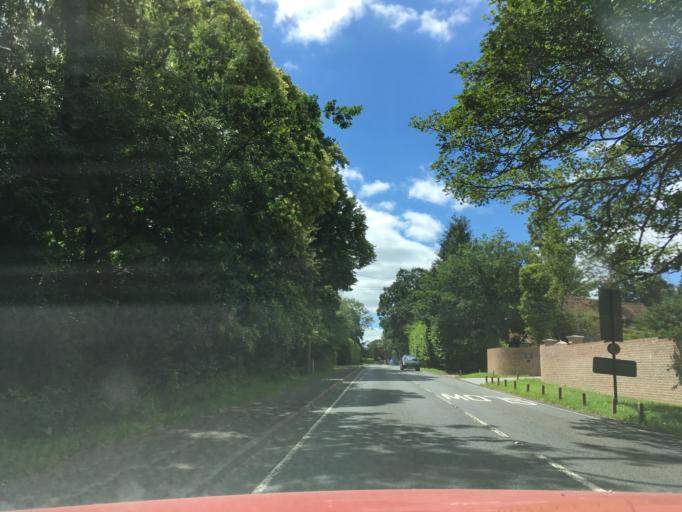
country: GB
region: England
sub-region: Hampshire
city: Highclere
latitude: 51.3414
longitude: -1.3738
